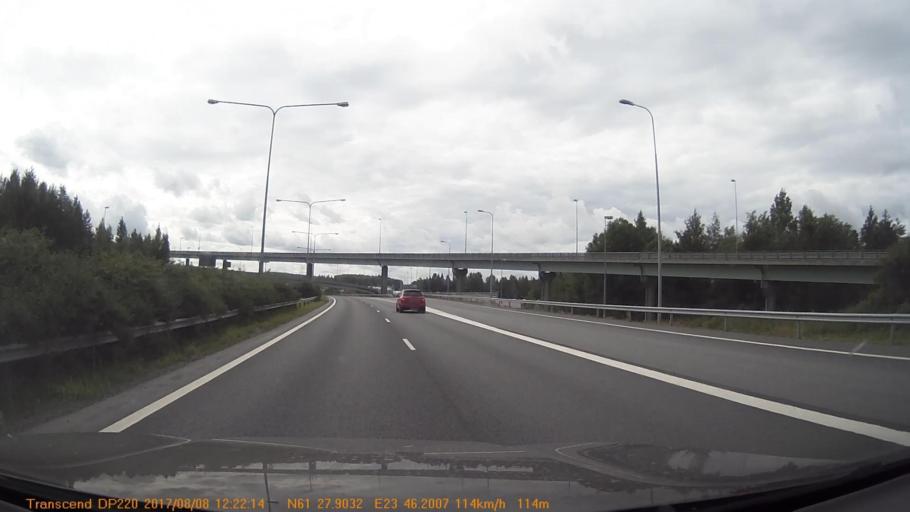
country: FI
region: Pirkanmaa
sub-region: Tampere
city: Tampere
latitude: 61.4646
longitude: 23.7699
